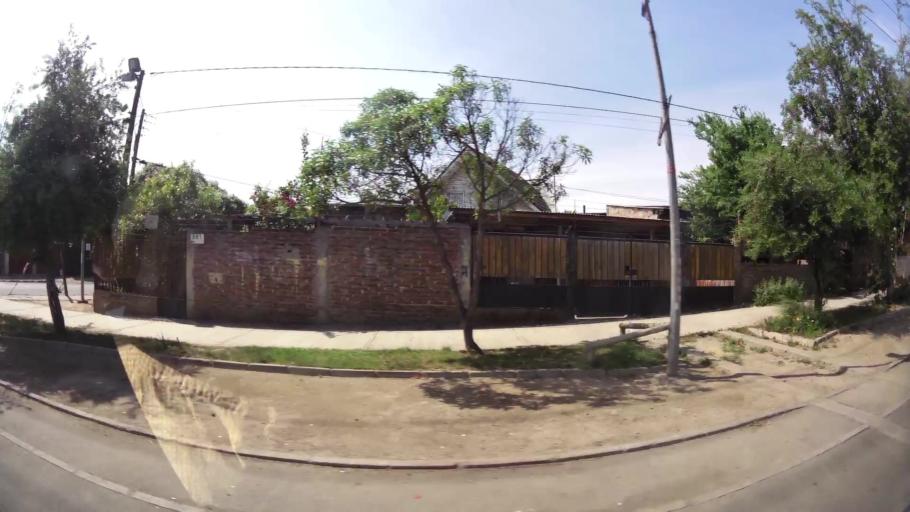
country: CL
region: Santiago Metropolitan
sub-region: Provincia de Santiago
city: Lo Prado
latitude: -33.4425
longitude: -70.7309
